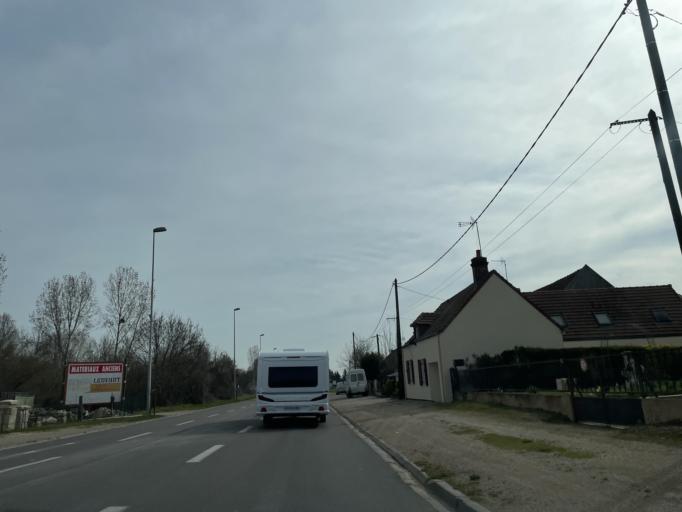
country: FR
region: Champagne-Ardenne
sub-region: Departement de l'Aube
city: Romilly-sur-Seine
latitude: 48.5153
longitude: 3.6590
